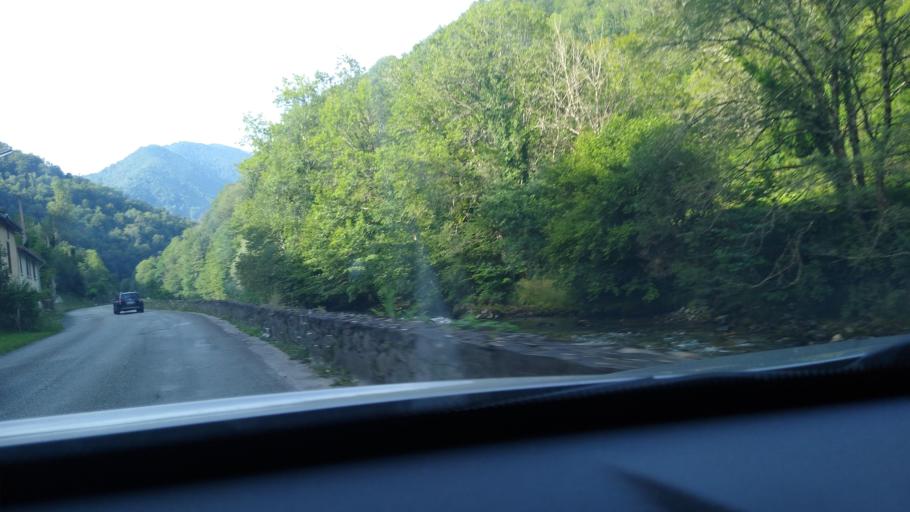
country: FR
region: Midi-Pyrenees
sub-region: Departement de l'Ariege
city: Saint-Girons
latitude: 42.8595
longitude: 1.1980
